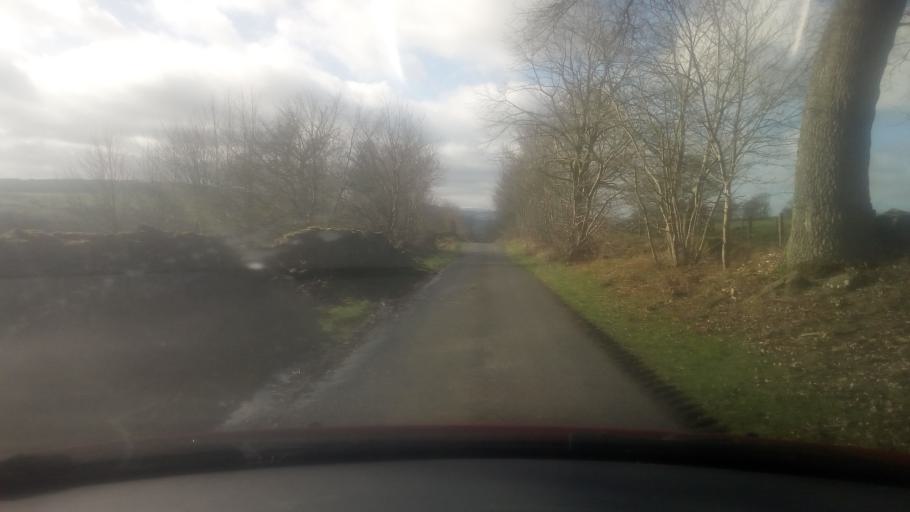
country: GB
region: Scotland
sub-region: The Scottish Borders
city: Jedburgh
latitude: 55.5224
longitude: -2.5762
